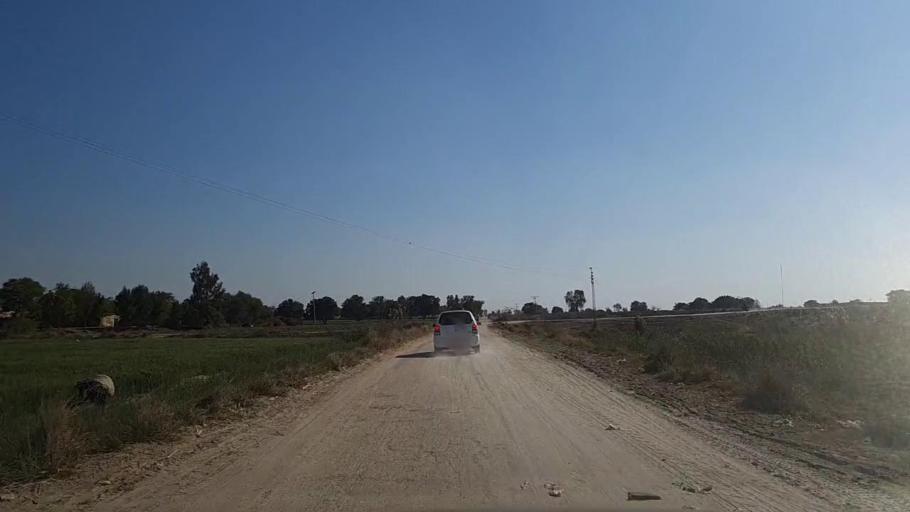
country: PK
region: Sindh
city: Nawabshah
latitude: 26.2327
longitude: 68.4265
